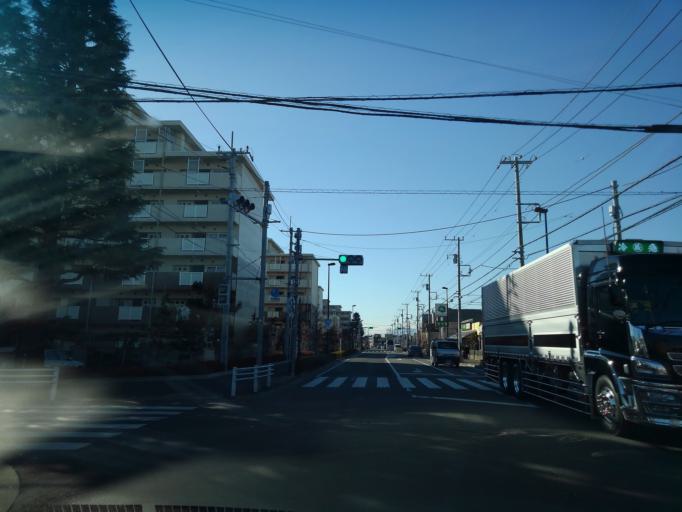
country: JP
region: Tokyo
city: Hino
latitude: 35.7132
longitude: 139.3800
